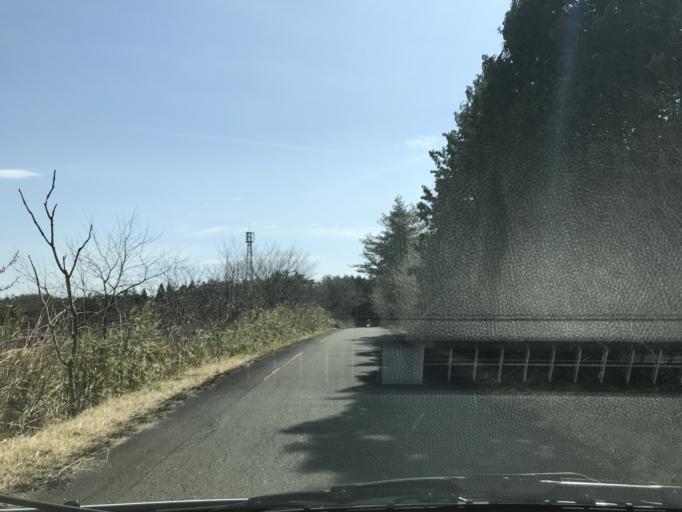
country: JP
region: Iwate
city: Ichinoseki
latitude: 38.8358
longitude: 141.1187
